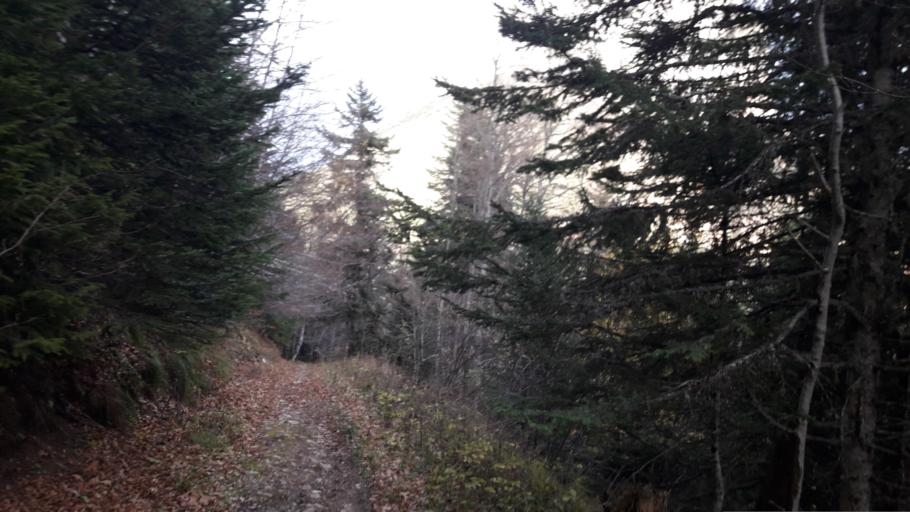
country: FR
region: Rhone-Alpes
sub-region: Departement de l'Isere
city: Bernin
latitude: 45.2978
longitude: 5.8364
